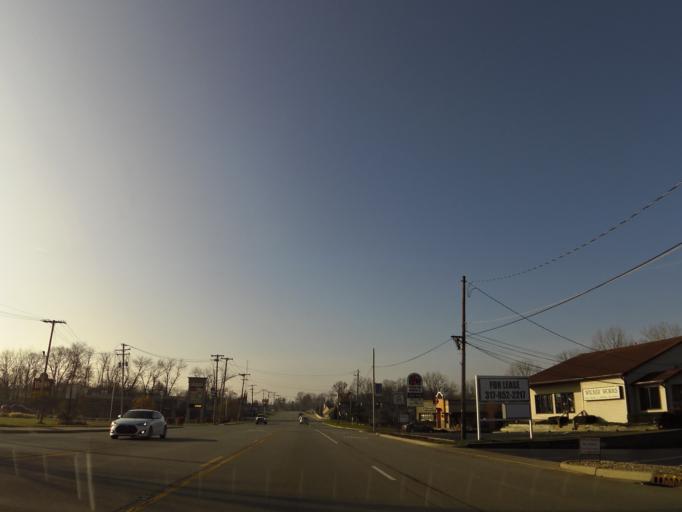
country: US
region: Indiana
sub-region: Hendricks County
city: Brownsburg
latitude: 39.8555
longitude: -86.3930
